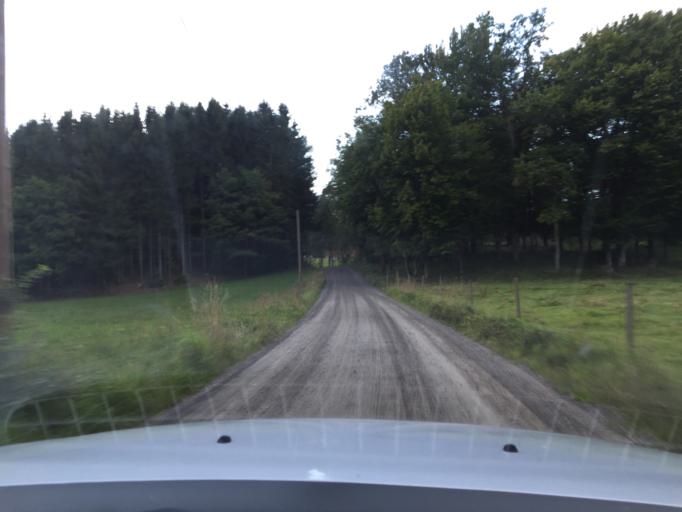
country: SE
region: Skane
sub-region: Hassleholms Kommun
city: Sosdala
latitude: 56.0596
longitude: 13.6636
